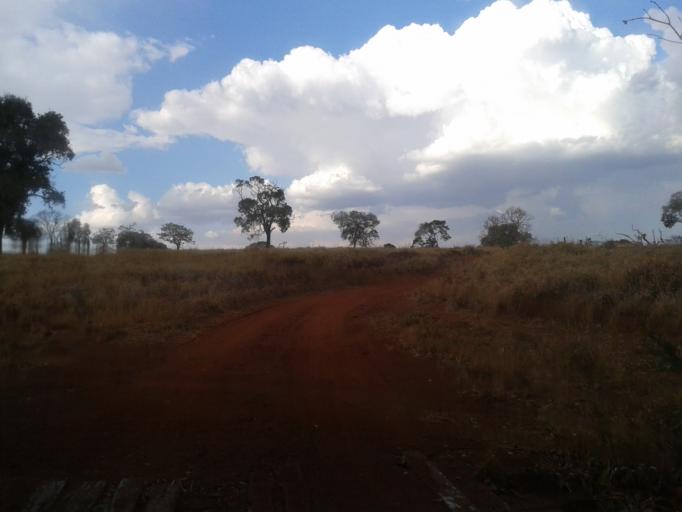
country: BR
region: Minas Gerais
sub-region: Santa Vitoria
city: Santa Vitoria
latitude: -19.1708
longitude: -49.9709
